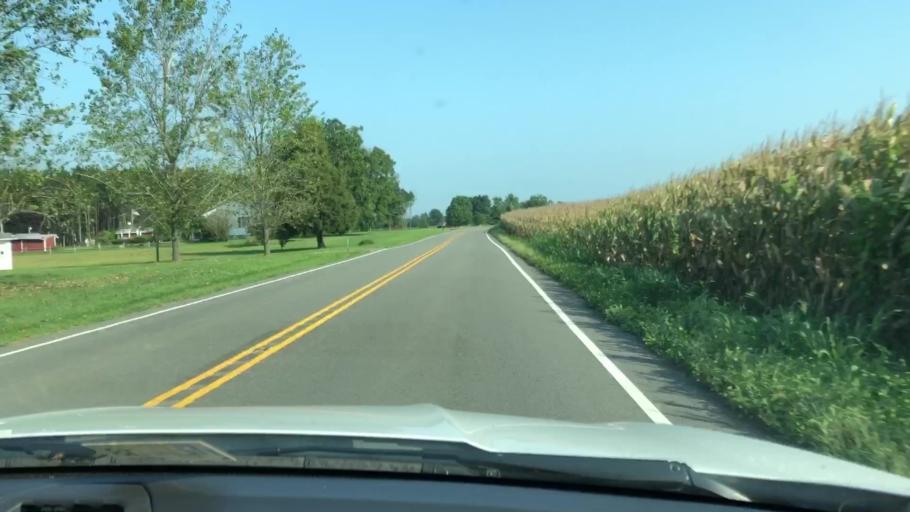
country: US
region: Virginia
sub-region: King William County
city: West Point
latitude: 37.6191
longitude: -76.7902
